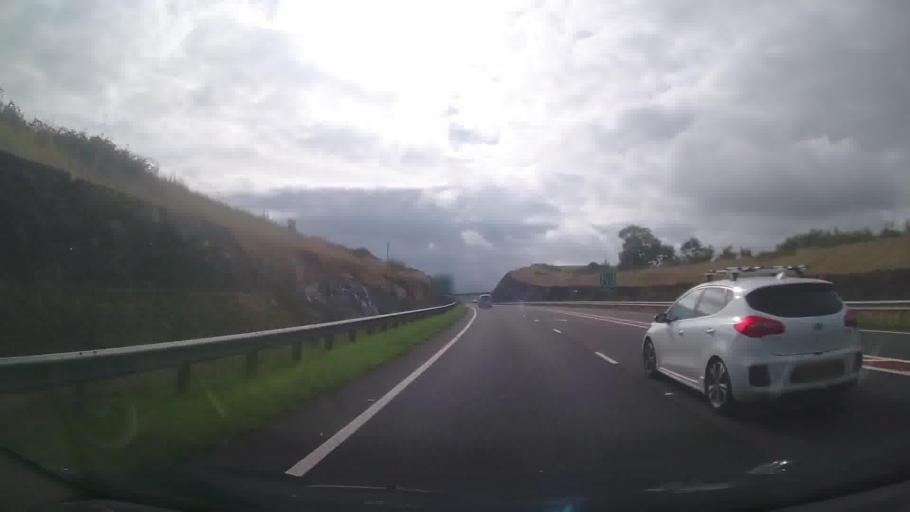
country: GB
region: Wales
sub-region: Carmarthenshire
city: Llanddowror
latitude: 51.8009
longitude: -4.5468
